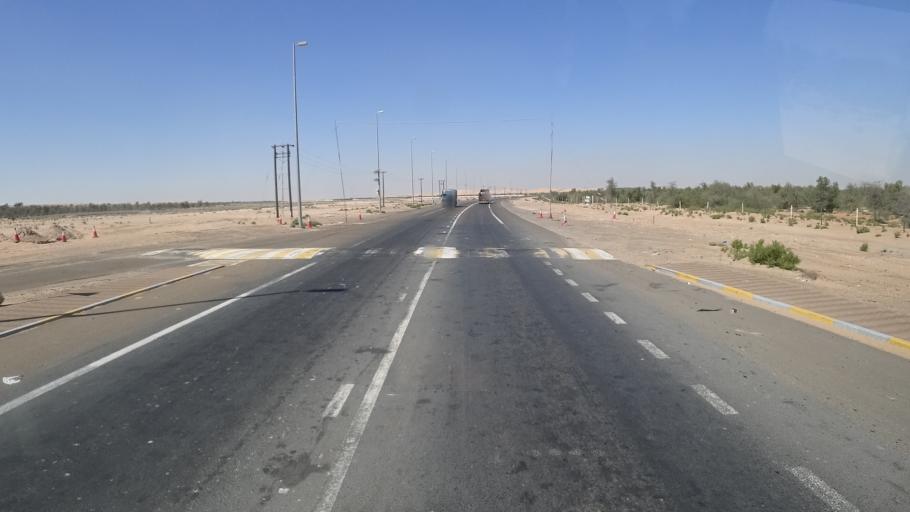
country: AE
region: Abu Dhabi
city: Al Ain
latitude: 24.1342
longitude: 55.0846
